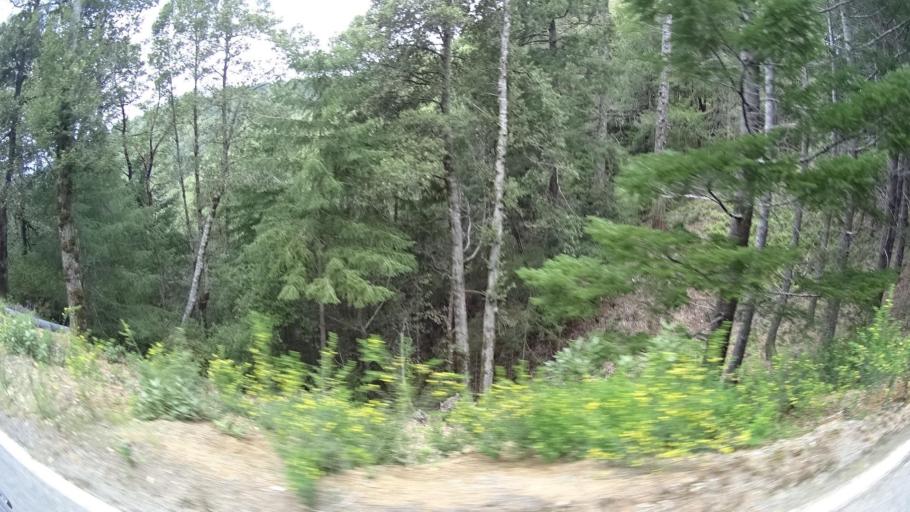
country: US
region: California
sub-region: Humboldt County
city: Redway
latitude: 40.0441
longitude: -124.0219
